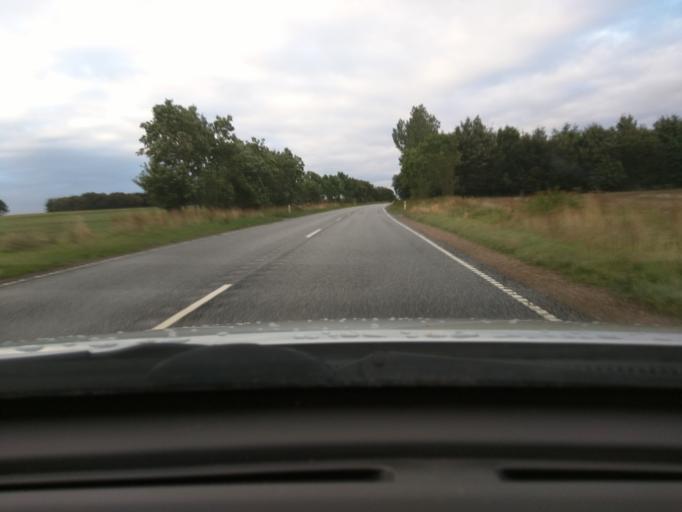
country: DK
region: Central Jutland
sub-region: Viborg Kommune
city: Viborg
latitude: 56.3808
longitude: 9.3803
